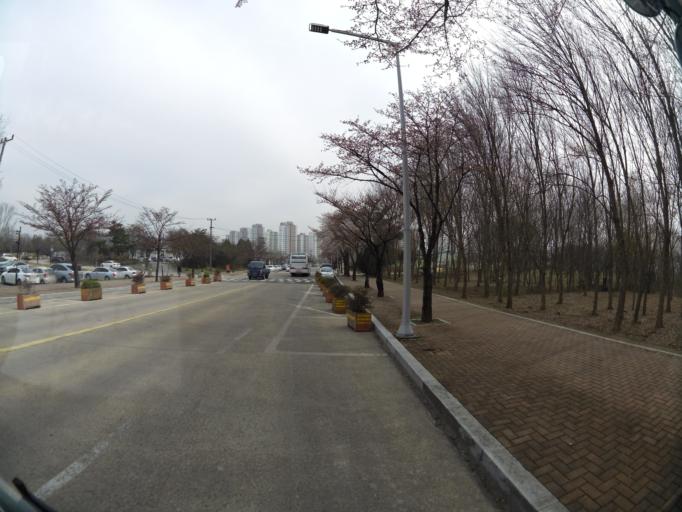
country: KR
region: Gyeongsangbuk-do
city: Gyeongsan-si
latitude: 35.8352
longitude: 128.7627
